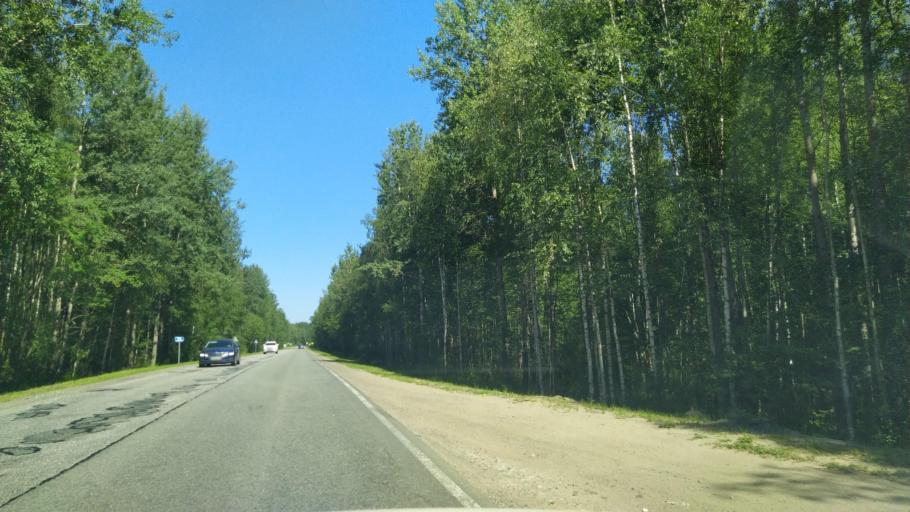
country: RU
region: Leningrad
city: Kirovsk
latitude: 59.9328
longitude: 30.9831
